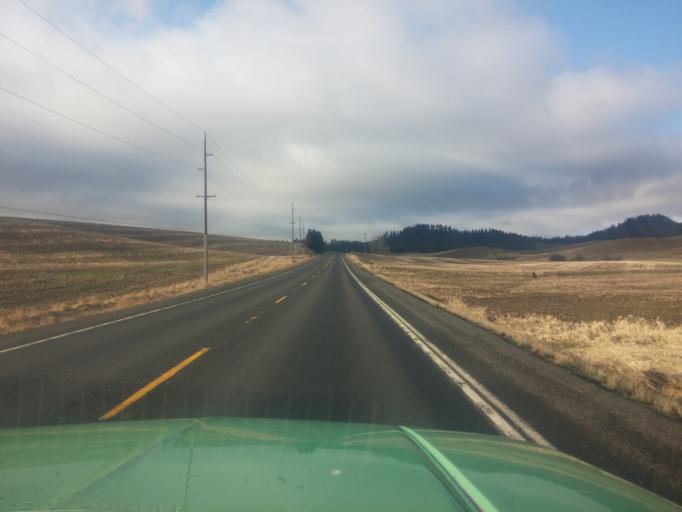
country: US
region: Idaho
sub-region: Latah County
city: Moscow
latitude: 46.8909
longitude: -116.9959
